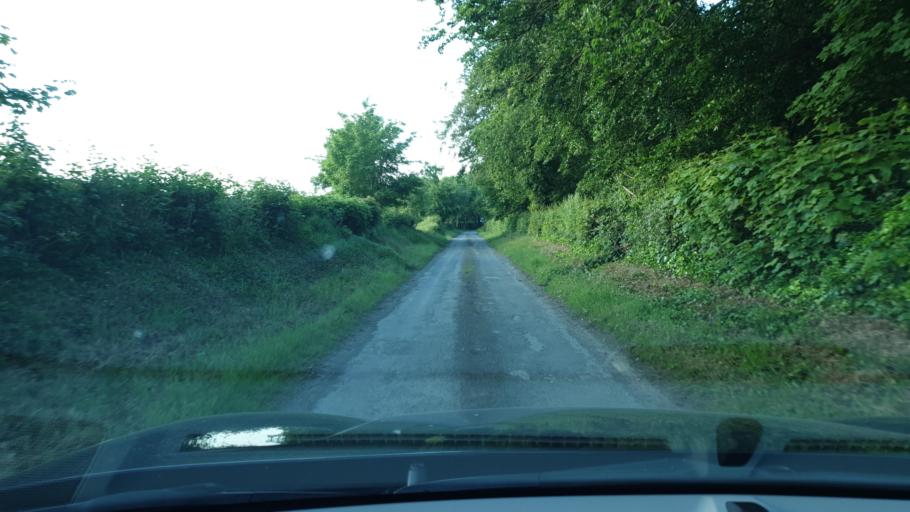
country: IE
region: Leinster
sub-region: An Mhi
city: Ashbourne
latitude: 53.4529
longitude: -6.4094
